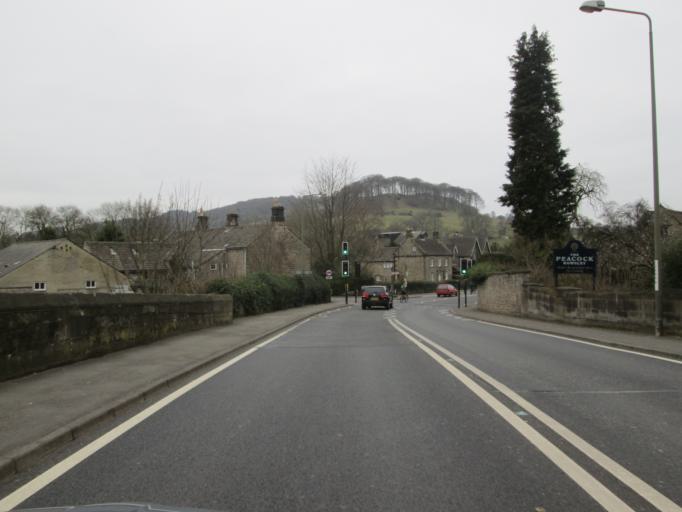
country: GB
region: England
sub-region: Derbyshire
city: Bakewell
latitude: 53.1895
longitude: -1.6173
